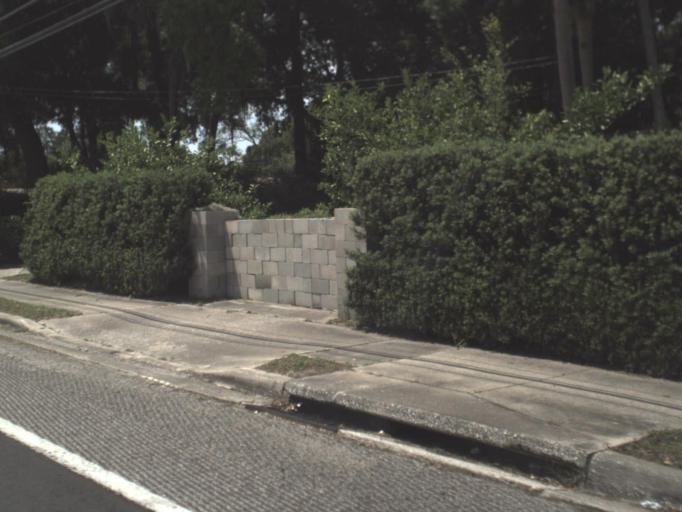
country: US
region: Florida
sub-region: Duval County
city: Jacksonville
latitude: 30.2347
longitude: -81.6192
